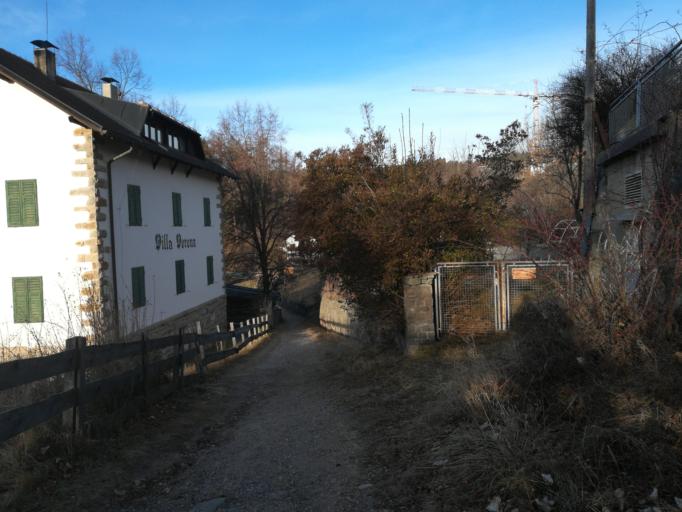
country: IT
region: Trentino-Alto Adige
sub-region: Bolzano
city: Collalbo
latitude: 46.5370
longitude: 11.4594
